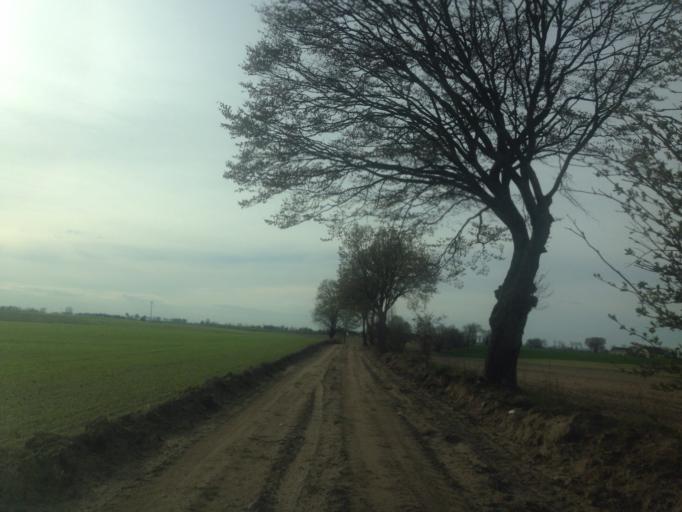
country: PL
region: Kujawsko-Pomorskie
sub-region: Powiat brodnicki
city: Jablonowo Pomorskie
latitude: 53.3754
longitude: 19.2413
